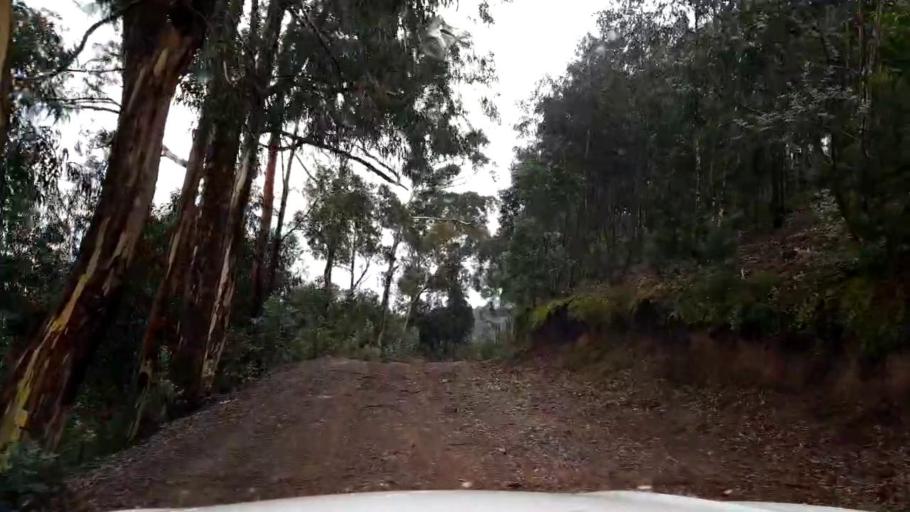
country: RW
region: Western Province
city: Kibuye
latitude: -2.0263
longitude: 29.4542
